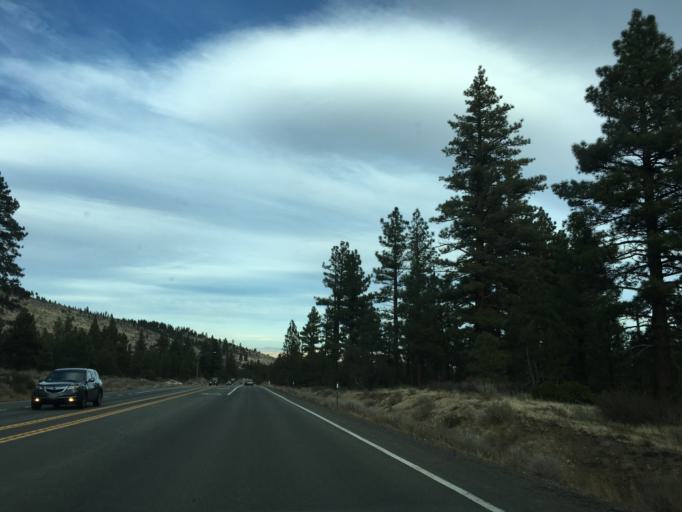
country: US
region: Nevada
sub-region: Washoe County
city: Incline Village
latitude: 39.3621
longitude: -119.8512
